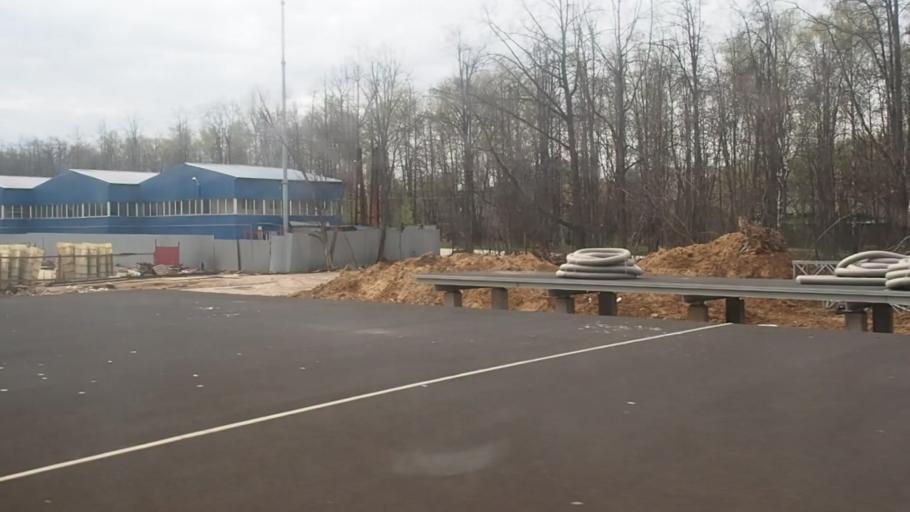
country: RU
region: Moskovskaya
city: Novoivanovskoye
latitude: 55.6993
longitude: 37.3415
